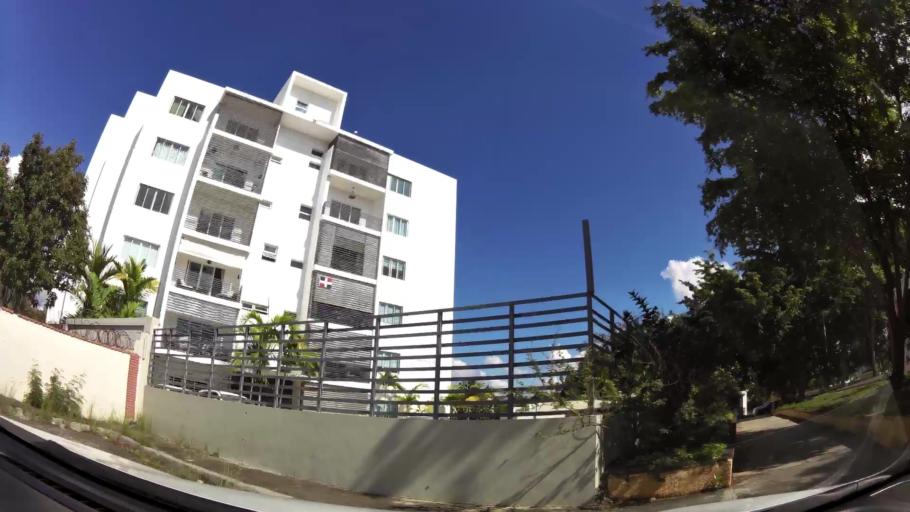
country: DO
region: Santiago
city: Santiago de los Caballeros
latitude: 19.4535
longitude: -70.6664
